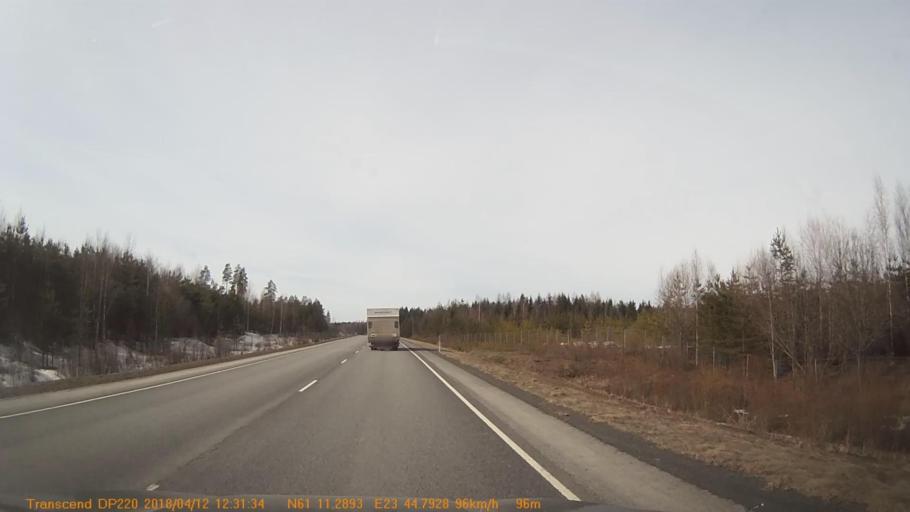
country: FI
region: Pirkanmaa
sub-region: Etelae-Pirkanmaa
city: Viiala
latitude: 61.1882
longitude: 23.7458
